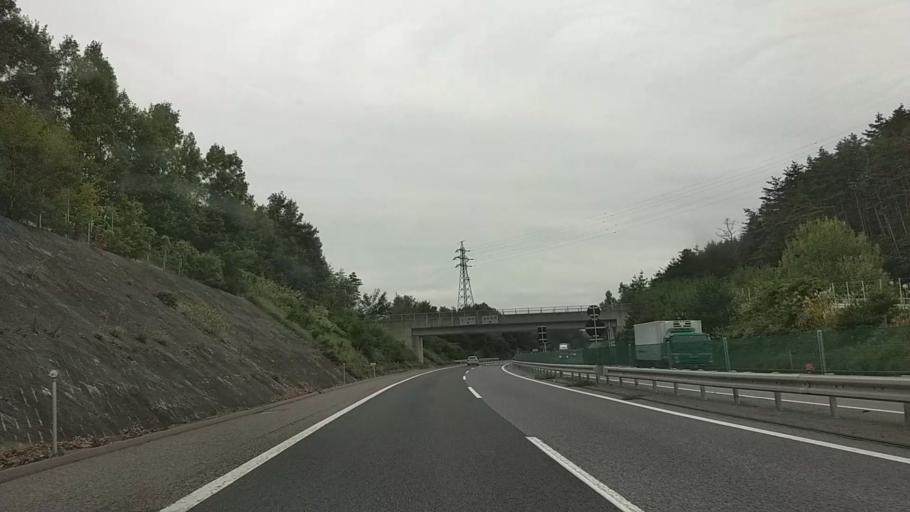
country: JP
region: Nagano
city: Hotaka
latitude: 36.4226
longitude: 138.0083
